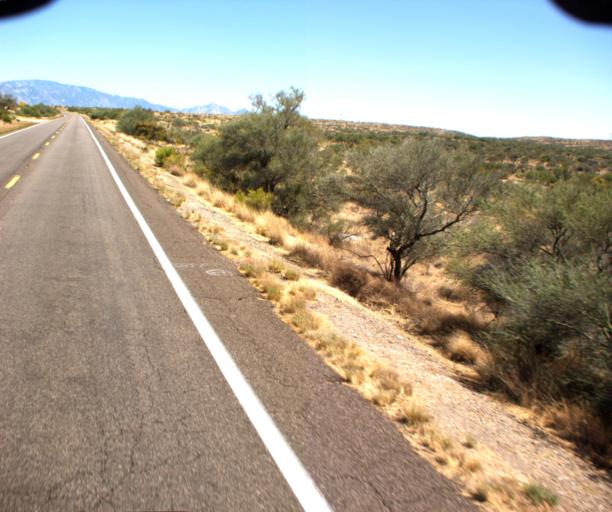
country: US
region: Arizona
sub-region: Pima County
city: Catalina
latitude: 32.6254
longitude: -110.9994
